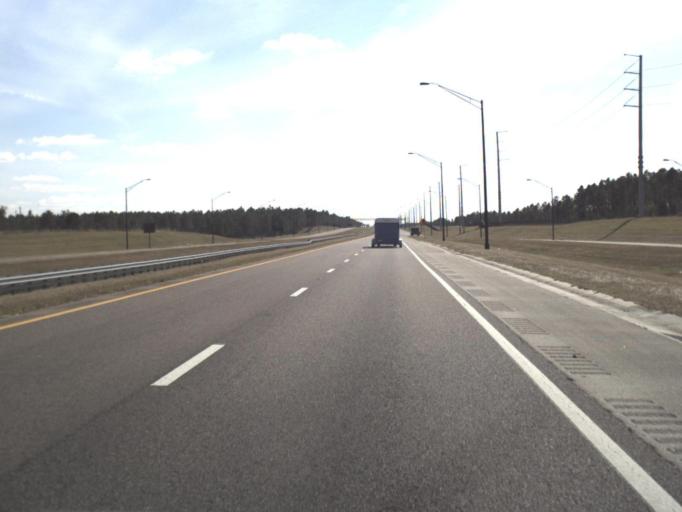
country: US
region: Florida
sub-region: Polk County
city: Citrus Ridge
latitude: 28.4148
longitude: -81.6300
